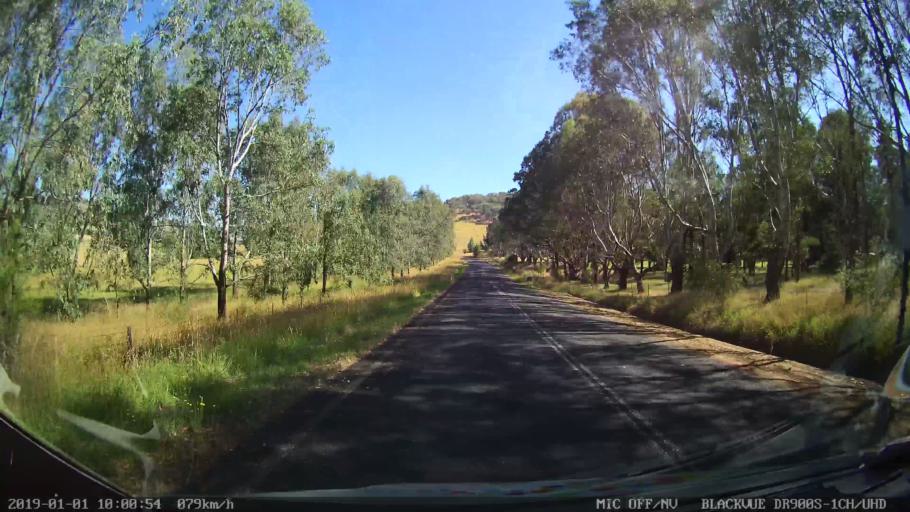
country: AU
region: New South Wales
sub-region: Snowy River
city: Jindabyne
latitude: -36.1971
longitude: 148.1028
